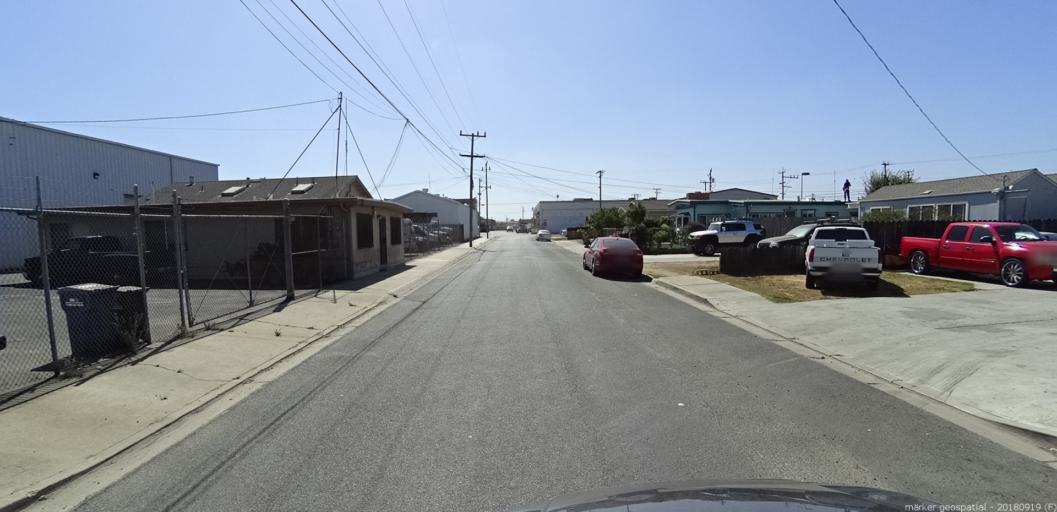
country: US
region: California
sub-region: Monterey County
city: Castroville
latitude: 36.7627
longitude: -121.7466
